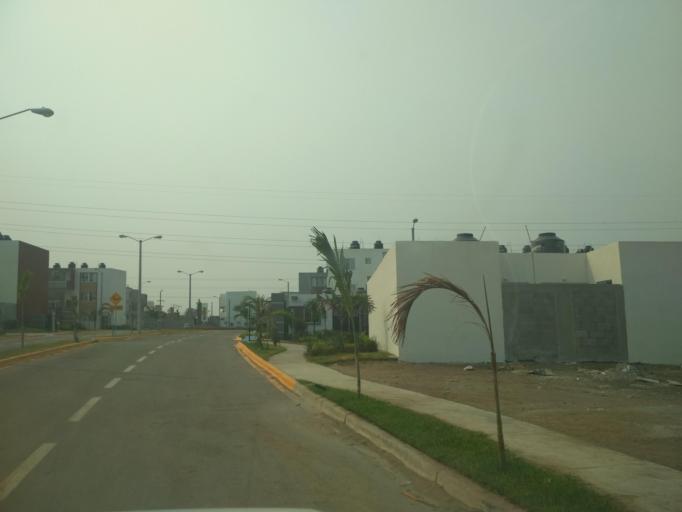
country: MX
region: Veracruz
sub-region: Veracruz
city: Las Amapolas
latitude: 19.1513
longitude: -96.2321
